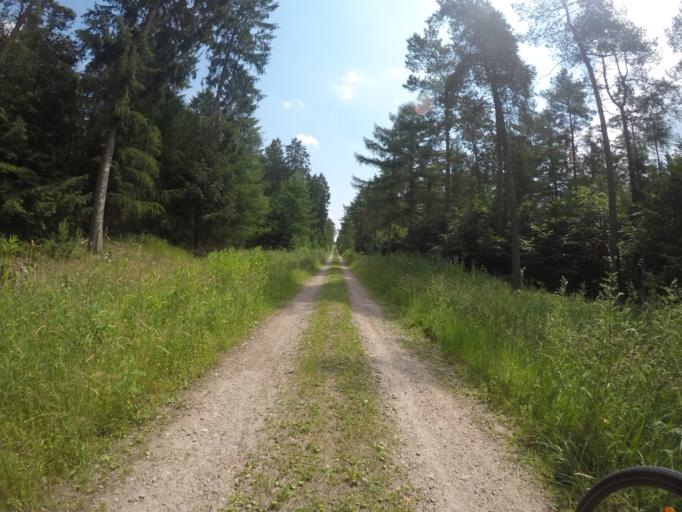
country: DE
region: Lower Saxony
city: Jesteburg
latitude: 53.2572
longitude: 9.9352
